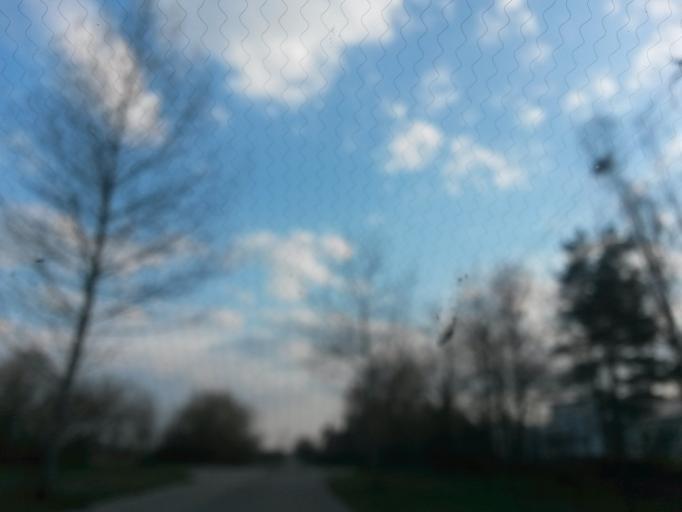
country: DE
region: Brandenburg
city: Strausberg
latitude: 52.5925
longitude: 13.9242
